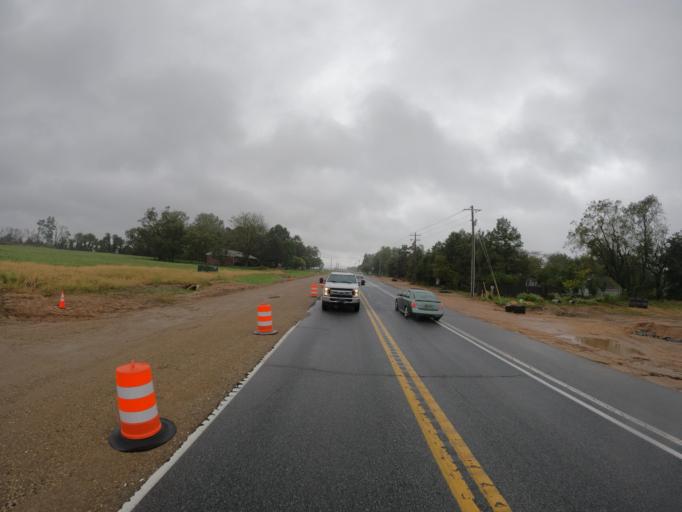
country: US
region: Delaware
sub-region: Sussex County
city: Milton
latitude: 38.8042
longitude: -75.2742
